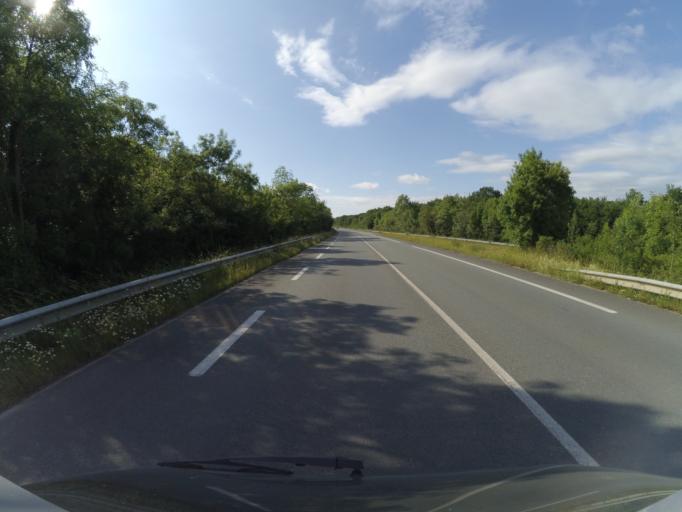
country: FR
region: Poitou-Charentes
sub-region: Departement de la Charente-Maritime
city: Saint-Agnant
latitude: 45.8347
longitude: -0.9399
